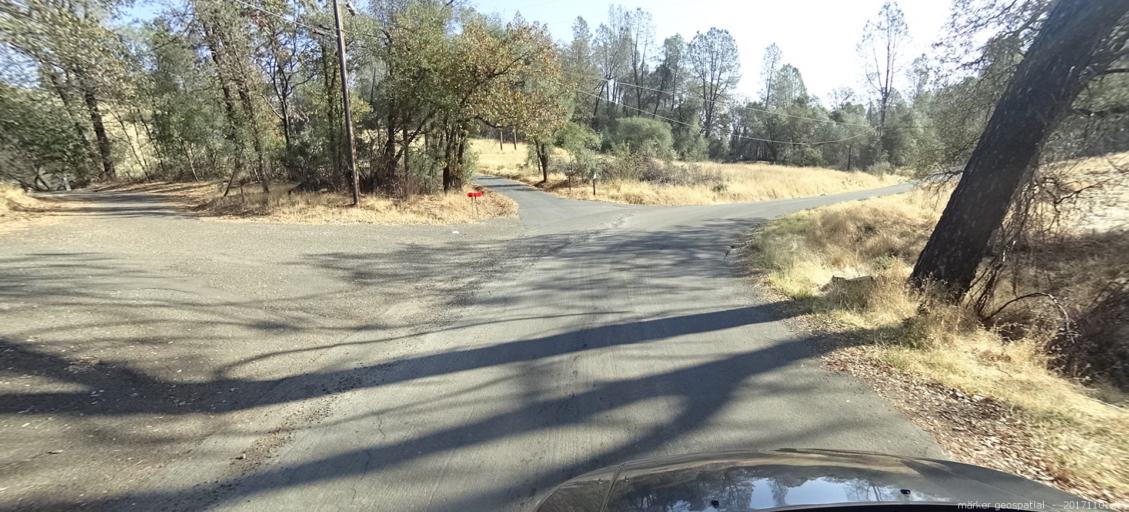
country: US
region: California
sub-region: Shasta County
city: Shasta Lake
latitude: 40.7079
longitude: -122.3214
